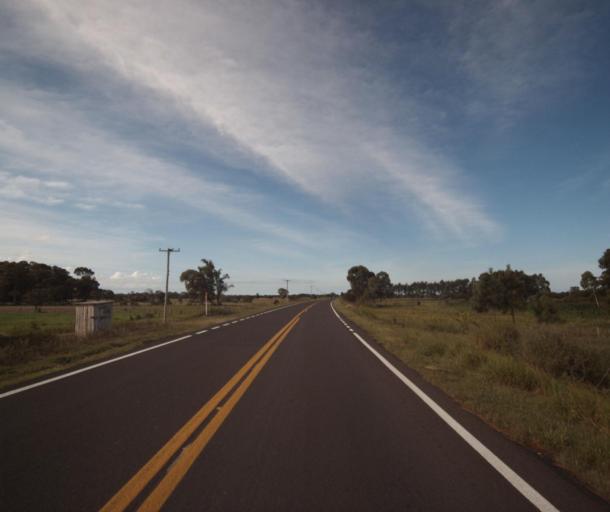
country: BR
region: Rio Grande do Sul
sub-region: Tapes
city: Tapes
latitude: -31.3210
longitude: -51.1233
